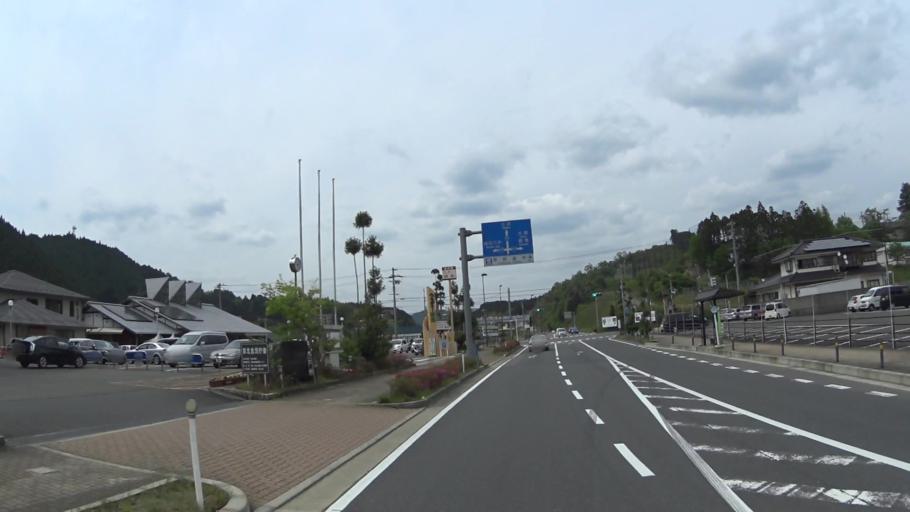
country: JP
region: Kyoto
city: Kameoka
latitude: 35.1554
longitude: 135.6338
